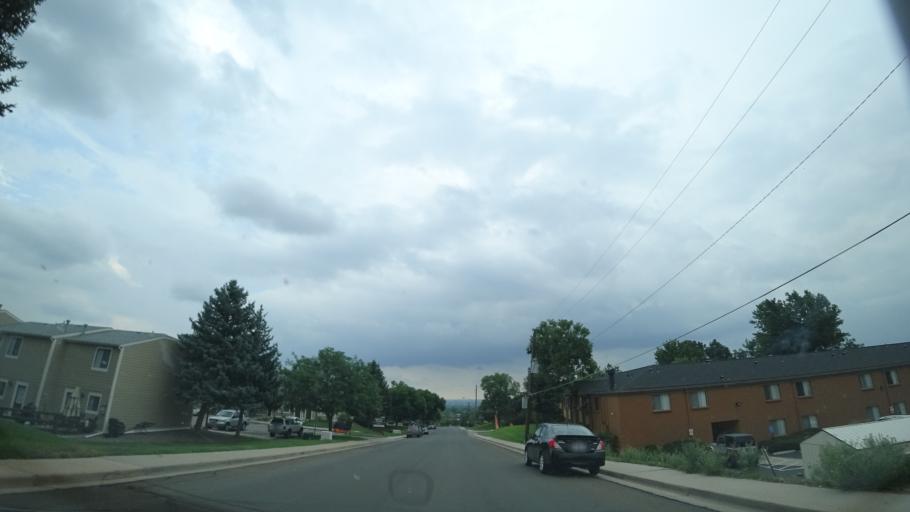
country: US
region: Colorado
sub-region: Jefferson County
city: West Pleasant View
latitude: 39.7098
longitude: -105.1421
